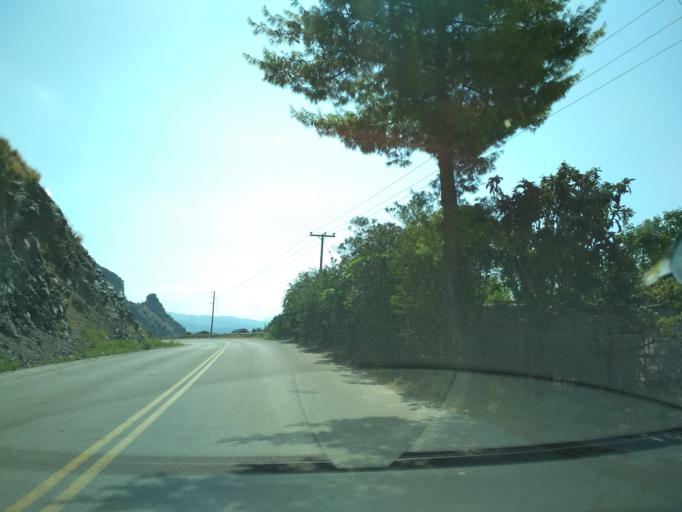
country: GR
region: Central Greece
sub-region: Nomos Evvoias
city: Oreoi
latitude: 38.8528
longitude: 23.1357
